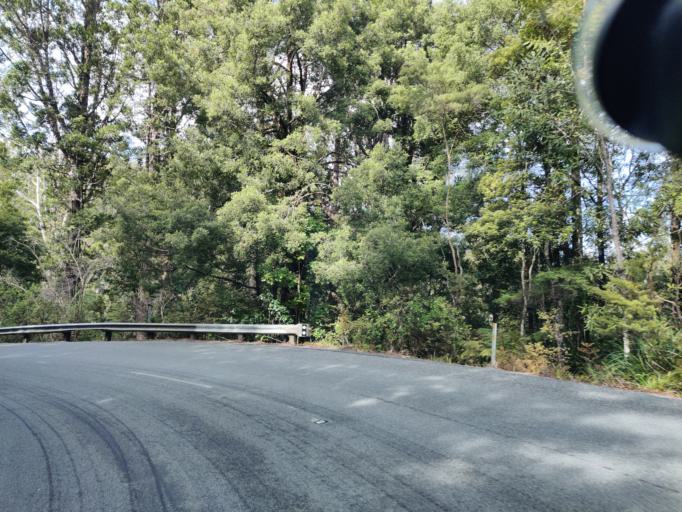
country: NZ
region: Northland
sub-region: Kaipara District
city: Dargaville
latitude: -35.6504
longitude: 173.5628
